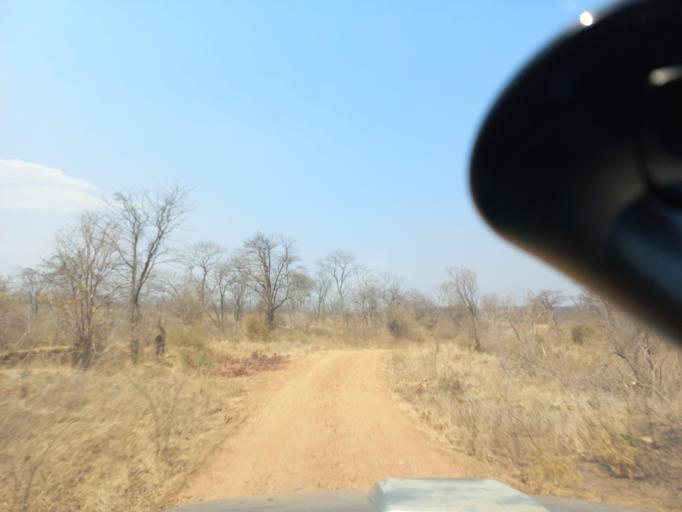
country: ZW
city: Chirundu
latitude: -15.9443
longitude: 28.7532
